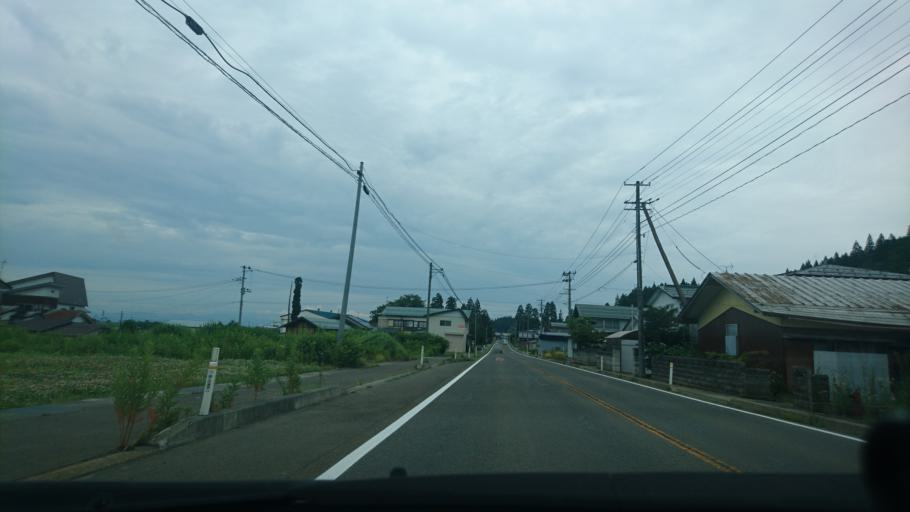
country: JP
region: Akita
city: Yokotemachi
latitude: 39.3652
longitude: 140.5664
